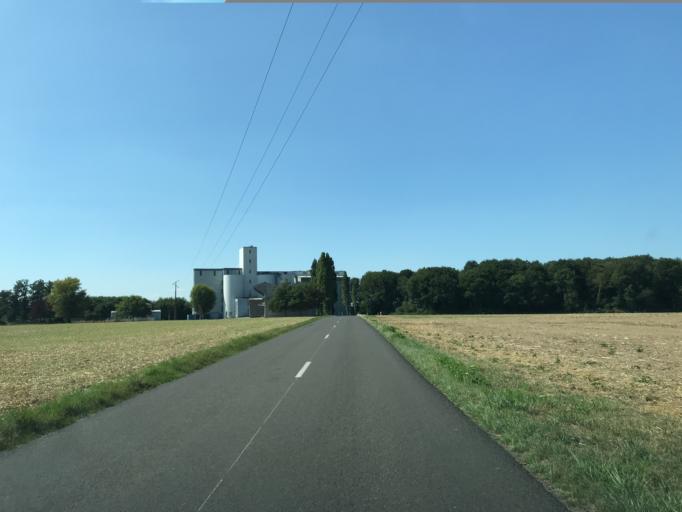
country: FR
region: Haute-Normandie
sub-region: Departement de l'Eure
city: Houlbec-Cocherel
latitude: 49.0938
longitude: 1.3550
